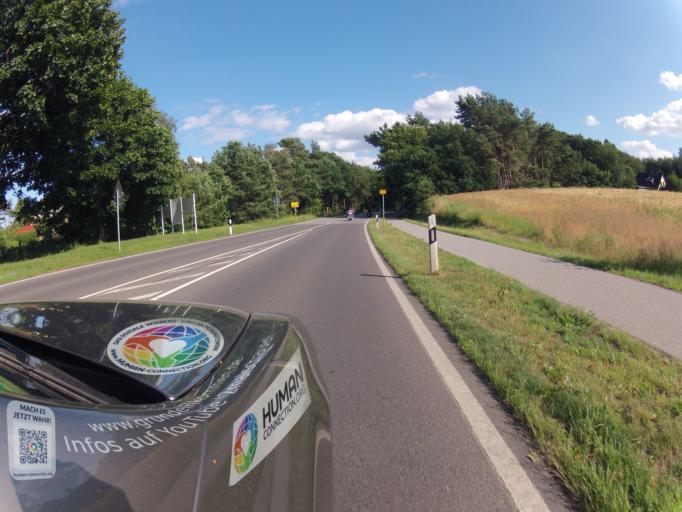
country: DE
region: Mecklenburg-Vorpommern
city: Loddin
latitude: 54.0099
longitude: 14.0554
